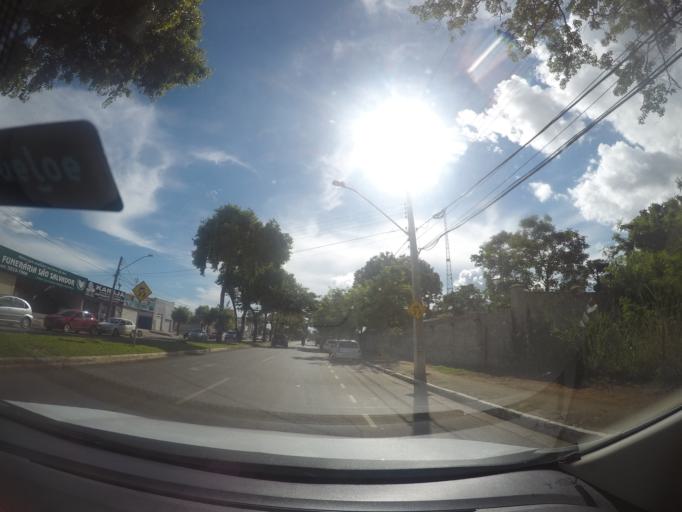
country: BR
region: Goias
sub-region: Goiania
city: Goiania
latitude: -16.6813
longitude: -49.3007
